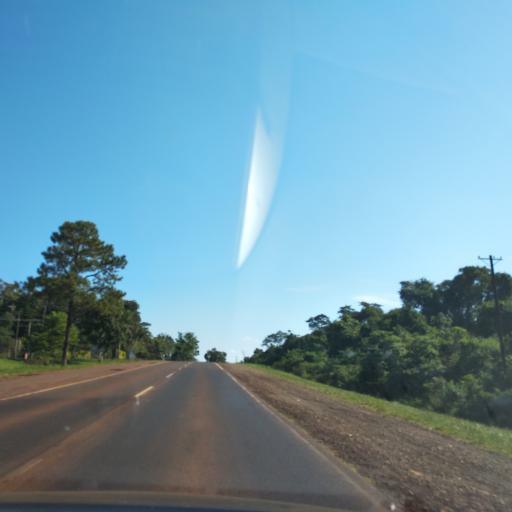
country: AR
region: Misiones
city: Jardin America
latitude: -27.0535
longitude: -55.2516
